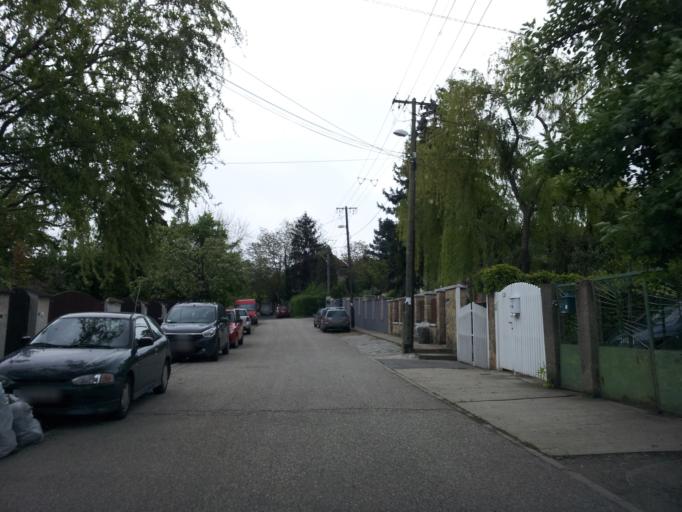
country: HU
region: Budapest
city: Budapest XXII. keruelet
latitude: 47.4405
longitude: 19.0201
